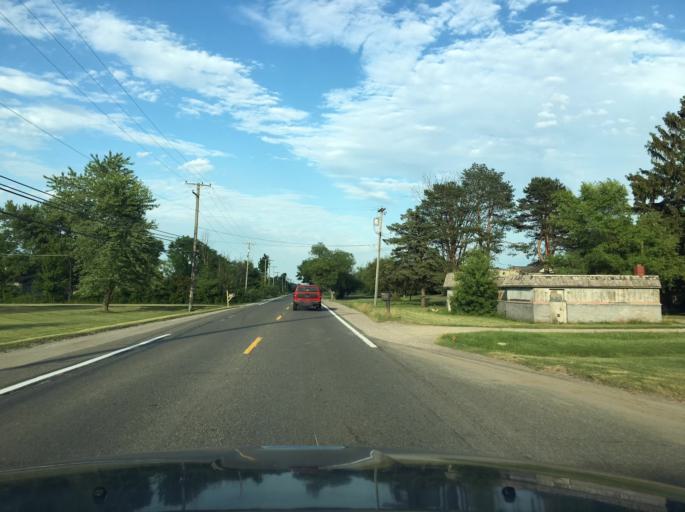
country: US
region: Michigan
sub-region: Macomb County
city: Shelby
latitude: 42.7163
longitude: -82.9506
